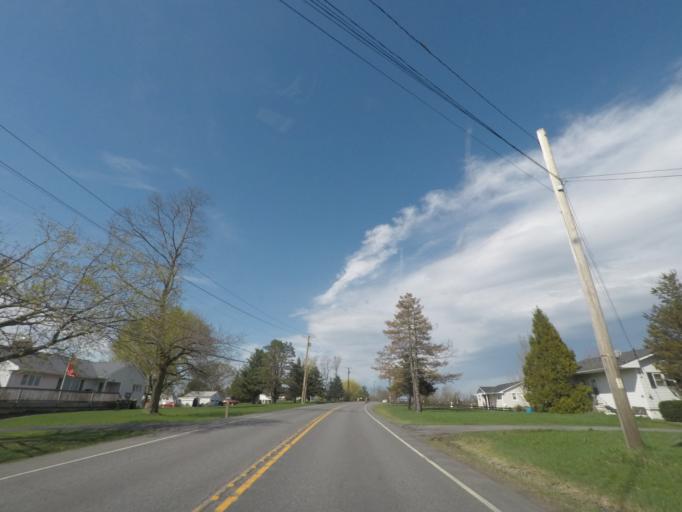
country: US
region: New York
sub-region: Greene County
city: Cairo
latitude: 42.4036
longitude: -74.0271
